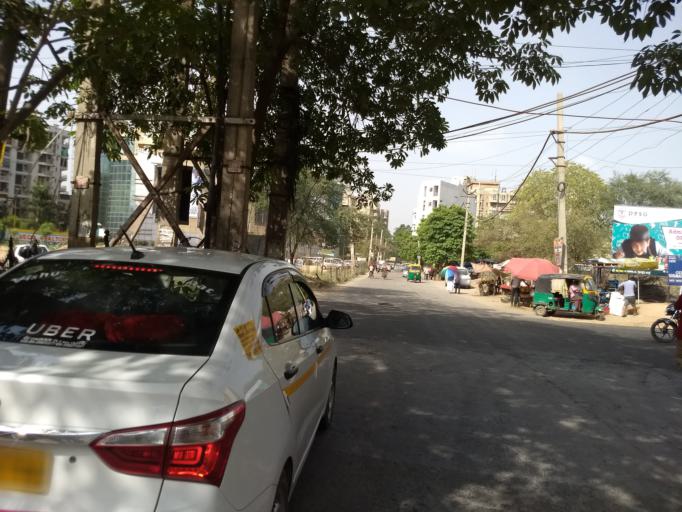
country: IN
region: Haryana
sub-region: Gurgaon
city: Gurgaon
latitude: 28.4498
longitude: 77.0778
